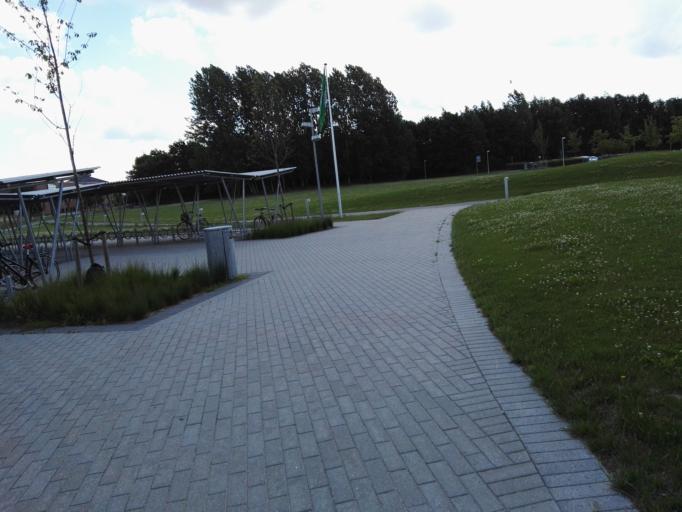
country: DK
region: Capital Region
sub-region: Ballerup Kommune
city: Ballerup
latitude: 55.7359
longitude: 12.3841
